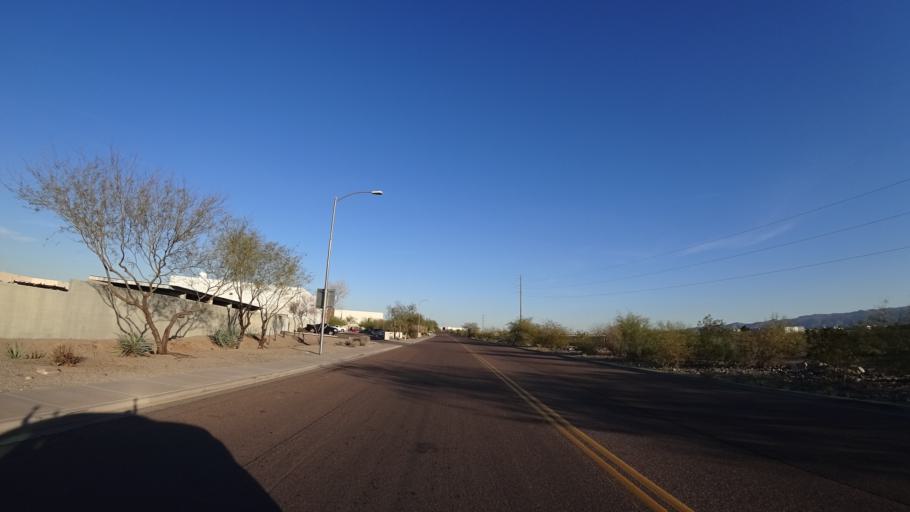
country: US
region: Arizona
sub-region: Maricopa County
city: Phoenix
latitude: 33.4206
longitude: -112.0512
